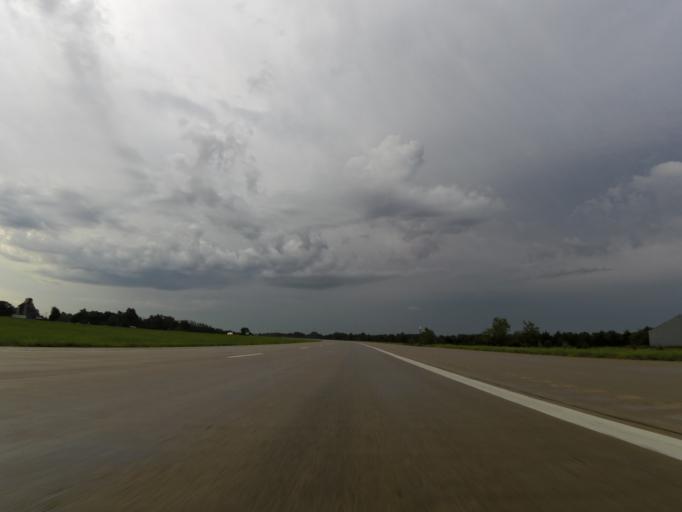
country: US
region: Kansas
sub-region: Reno County
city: South Hutchinson
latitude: 37.9703
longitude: -97.9354
